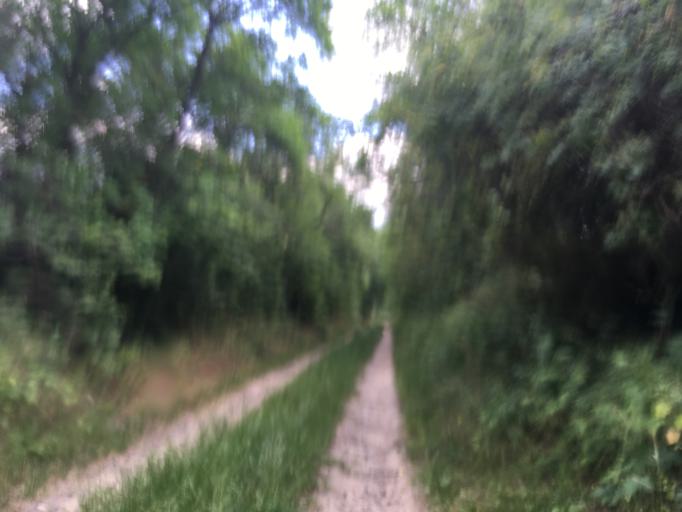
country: DE
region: Brandenburg
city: Buckow
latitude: 52.5824
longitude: 14.0565
